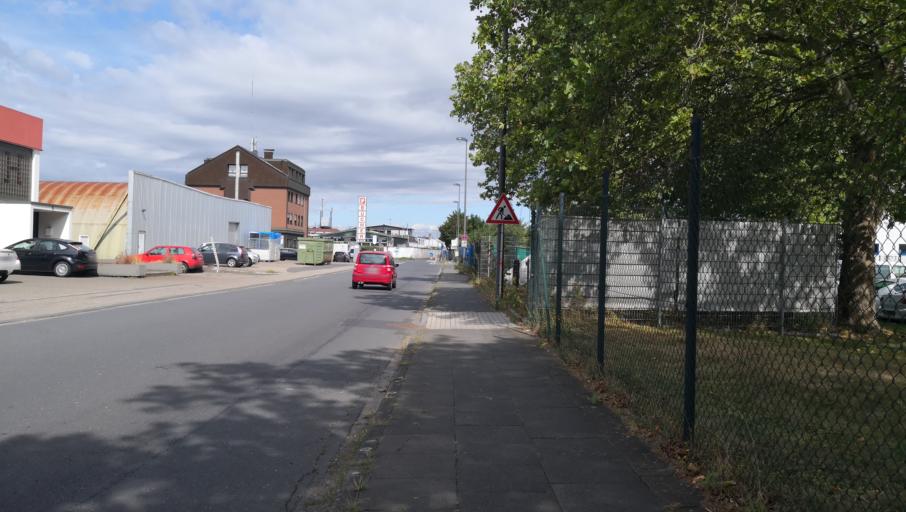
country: DE
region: North Rhine-Westphalia
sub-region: Regierungsbezirk Koln
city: Wahn-Heide
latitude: 50.8398
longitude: 7.1064
